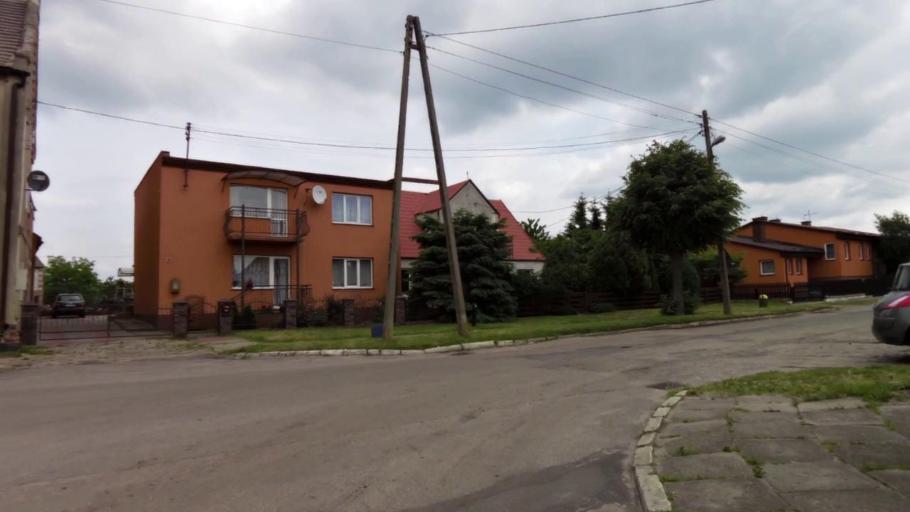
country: PL
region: West Pomeranian Voivodeship
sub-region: Powiat policki
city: Police
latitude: 53.5041
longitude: 14.7026
